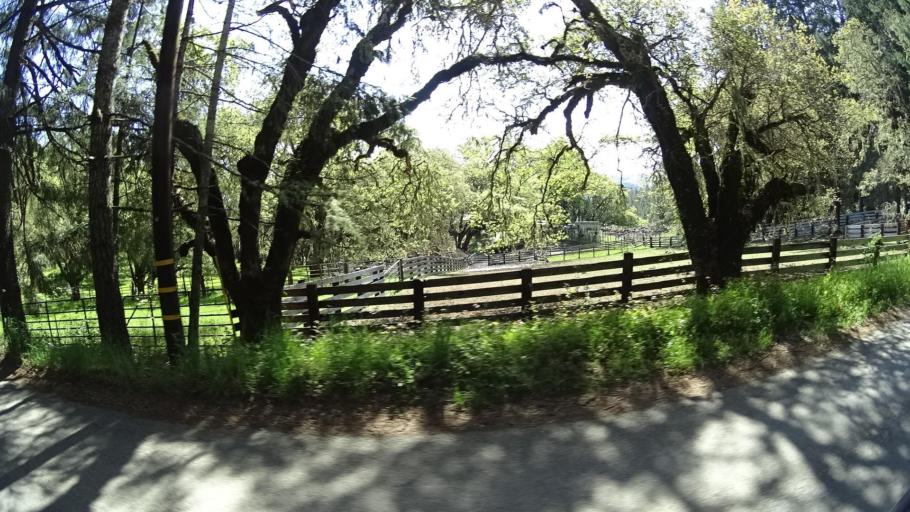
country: US
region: California
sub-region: Humboldt County
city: Redway
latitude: 40.0505
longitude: -123.6417
